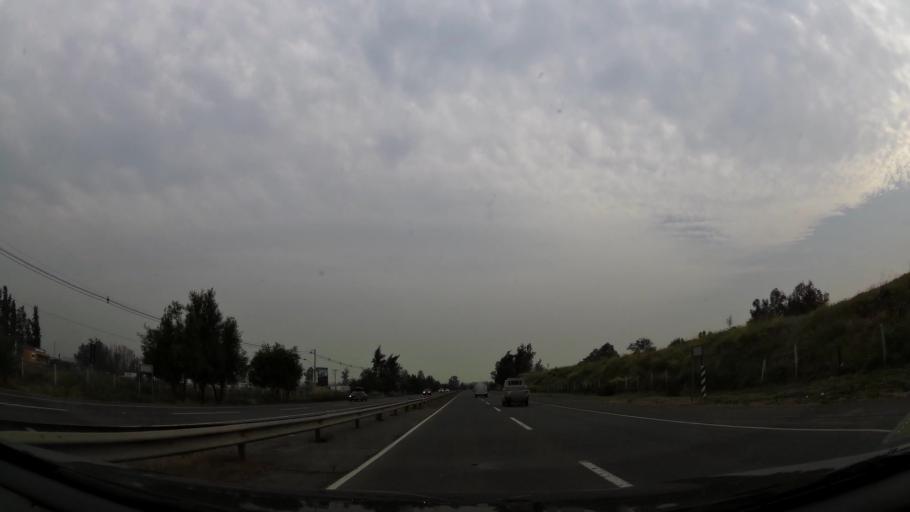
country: CL
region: Santiago Metropolitan
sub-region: Provincia de Chacabuco
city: Chicureo Abajo
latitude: -33.2260
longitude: -70.6834
